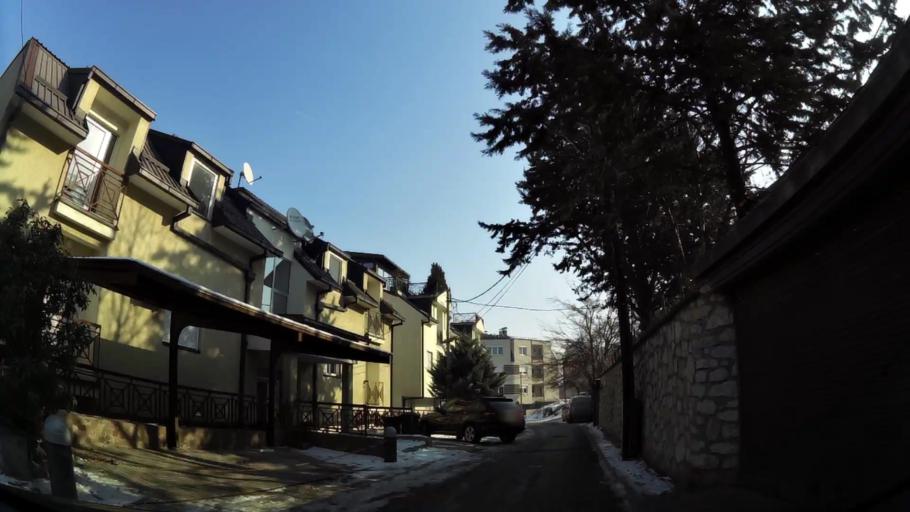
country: MK
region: Karpos
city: Skopje
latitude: 41.9820
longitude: 21.4241
